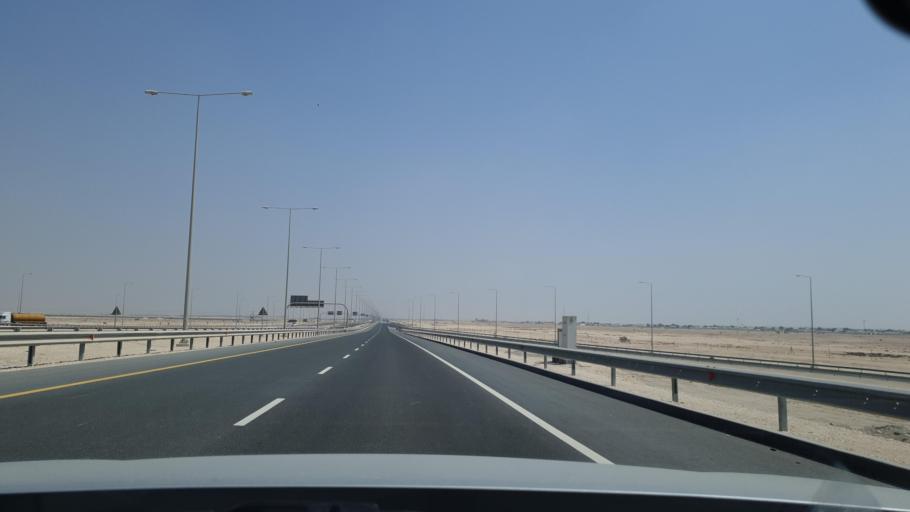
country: QA
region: Baladiyat az Za`ayin
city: Az Za`ayin
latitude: 25.6171
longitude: 51.3718
